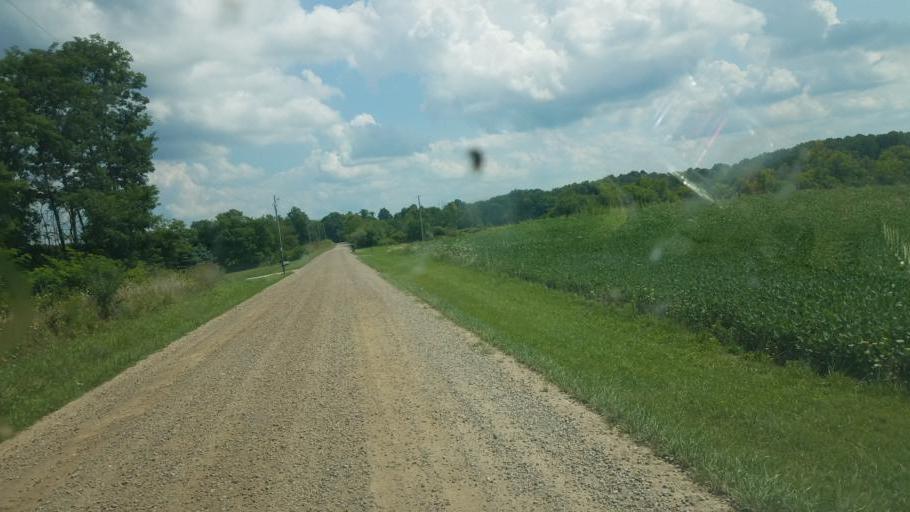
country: US
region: Ohio
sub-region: Knox County
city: Mount Vernon
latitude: 40.3714
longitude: -82.5993
